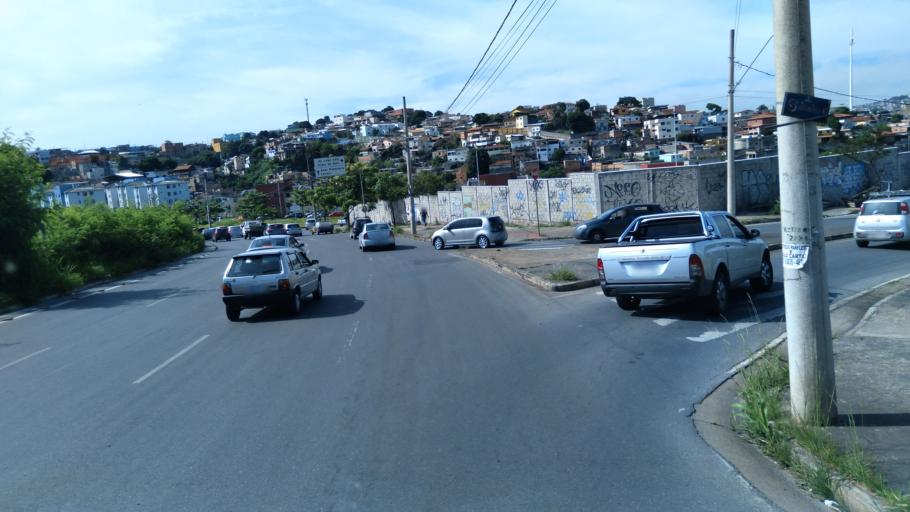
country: BR
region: Minas Gerais
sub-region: Belo Horizonte
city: Belo Horizonte
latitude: -19.8998
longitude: -43.9929
